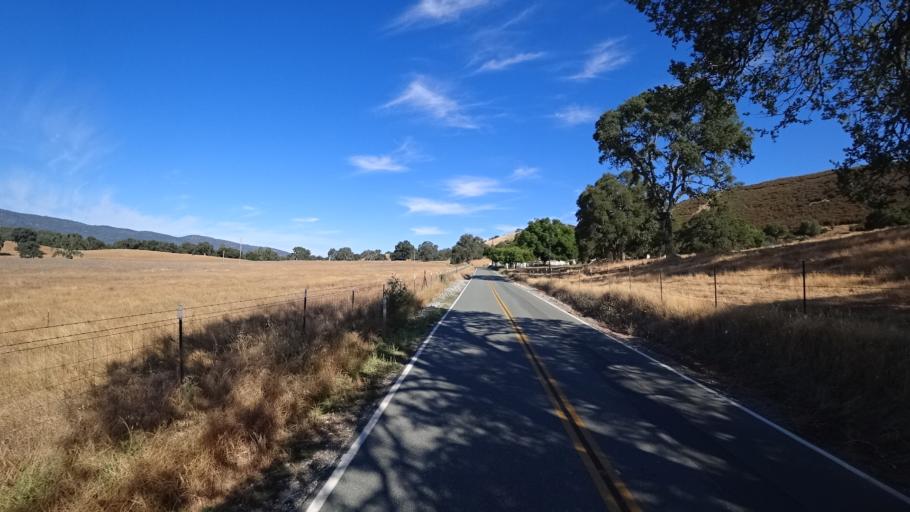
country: US
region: California
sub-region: Calaveras County
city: San Andreas
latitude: 38.1700
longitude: -120.6286
